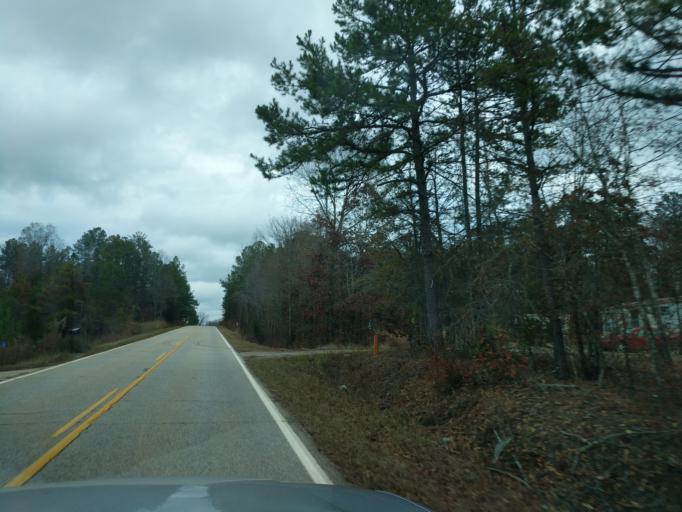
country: US
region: South Carolina
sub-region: Greenwood County
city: Ware Shoals
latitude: 34.3948
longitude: -82.1385
